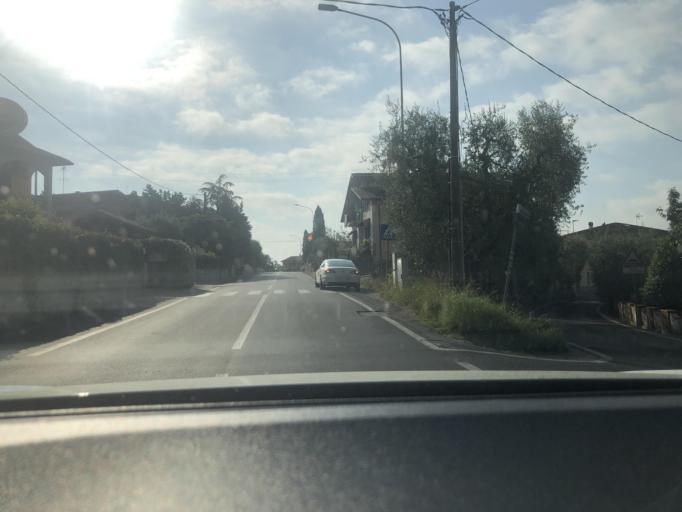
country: IT
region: Tuscany
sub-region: Provincia di Pistoia
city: San Rocco
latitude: 43.8033
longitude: 10.8532
